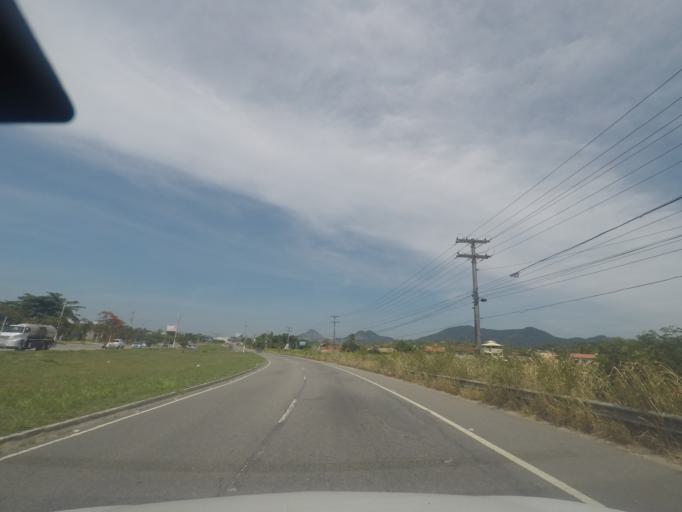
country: BR
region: Rio de Janeiro
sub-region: Marica
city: Marica
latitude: -22.9056
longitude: -42.8157
